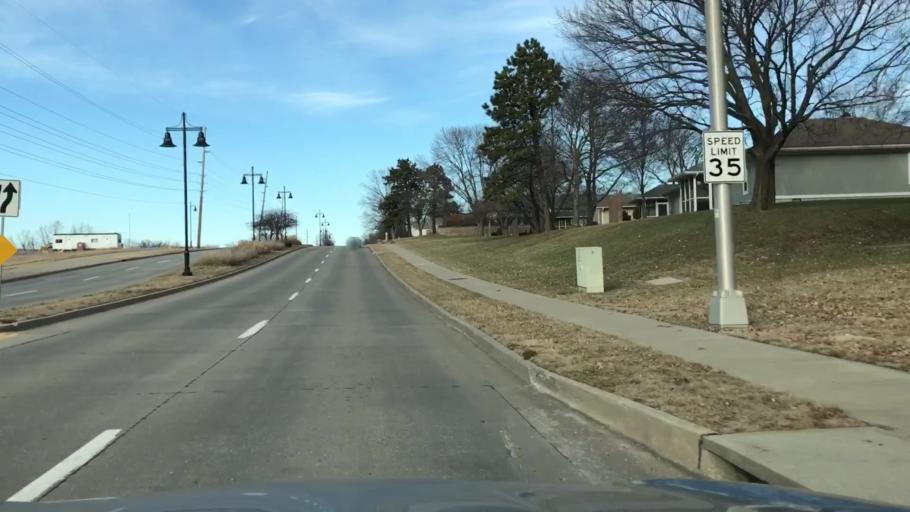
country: US
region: Missouri
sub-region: Jackson County
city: Lees Summit
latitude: 38.9155
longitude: -94.4133
